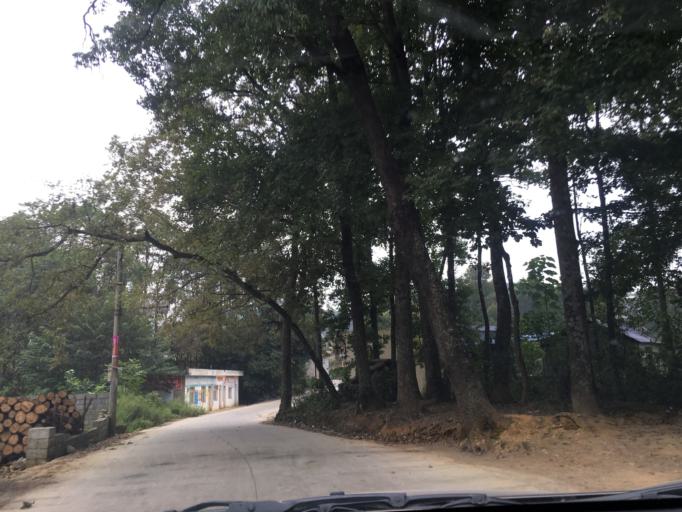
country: CN
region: Guangxi Zhuangzu Zizhiqu
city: Xinzhou
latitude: 25.5354
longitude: 105.6148
